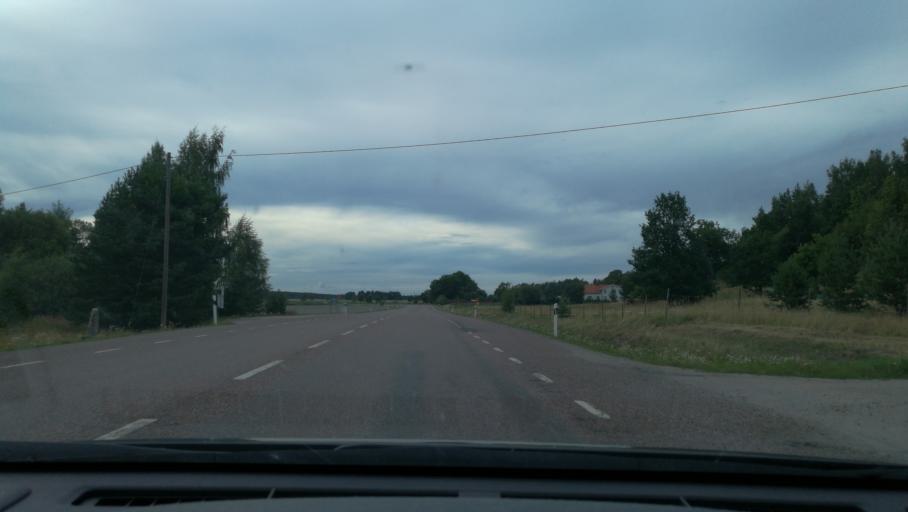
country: SE
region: Vaestmanland
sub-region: Kungsors Kommun
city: Kungsoer
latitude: 59.4295
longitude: 16.0872
